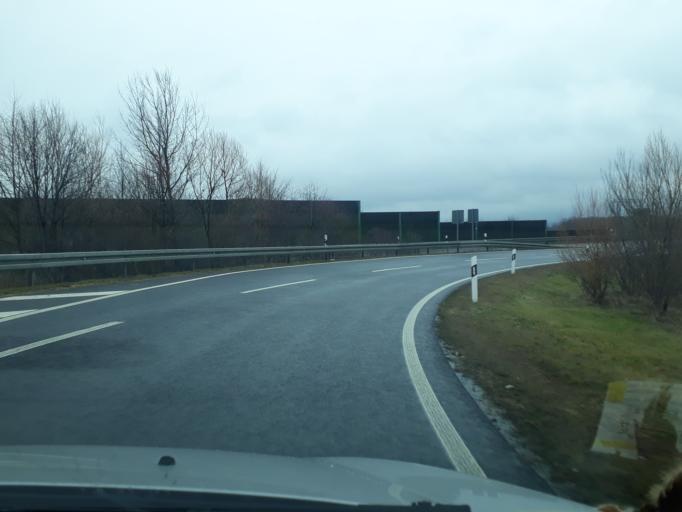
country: DE
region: Saxony
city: Bautzen
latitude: 51.1955
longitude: 14.4668
